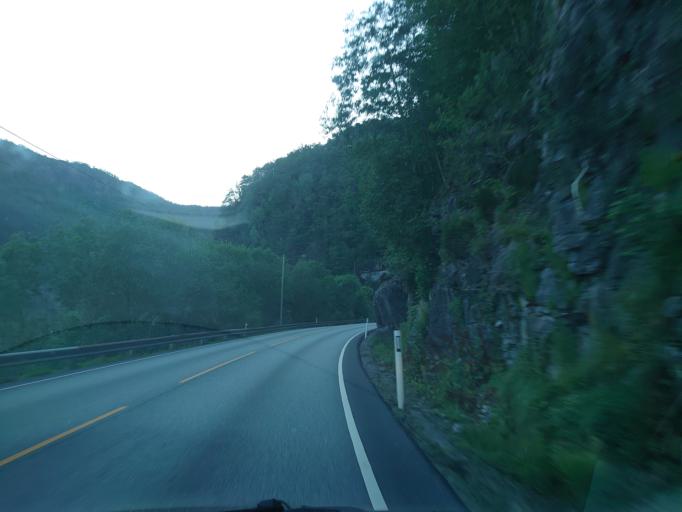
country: NO
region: Hordaland
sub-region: Osteroy
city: Lonevag
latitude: 60.6992
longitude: 5.5621
